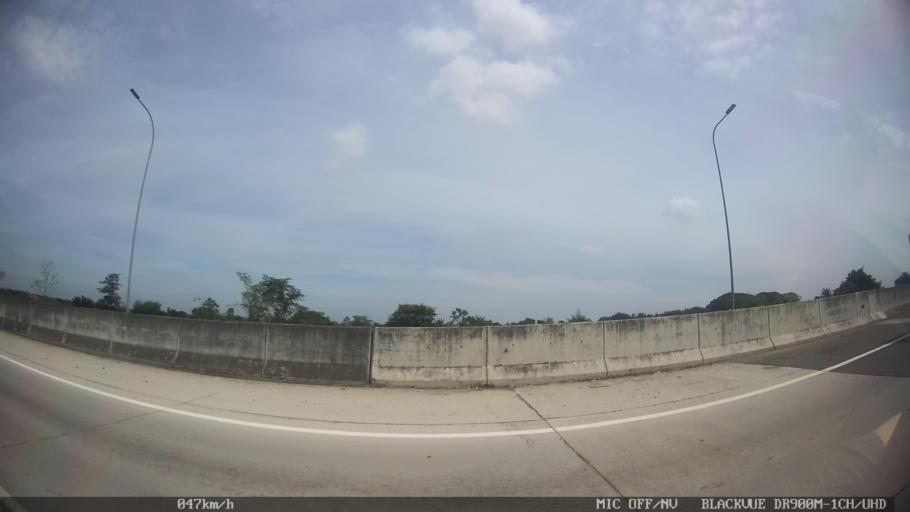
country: ID
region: North Sumatra
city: Medan
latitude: 3.6489
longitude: 98.6543
